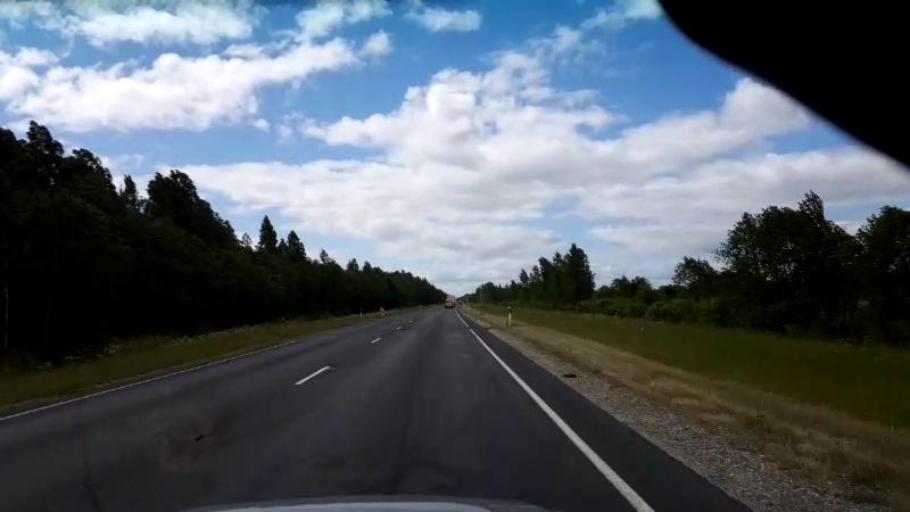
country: LV
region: Salacgrivas
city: Ainazi
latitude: 58.0059
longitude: 24.4859
